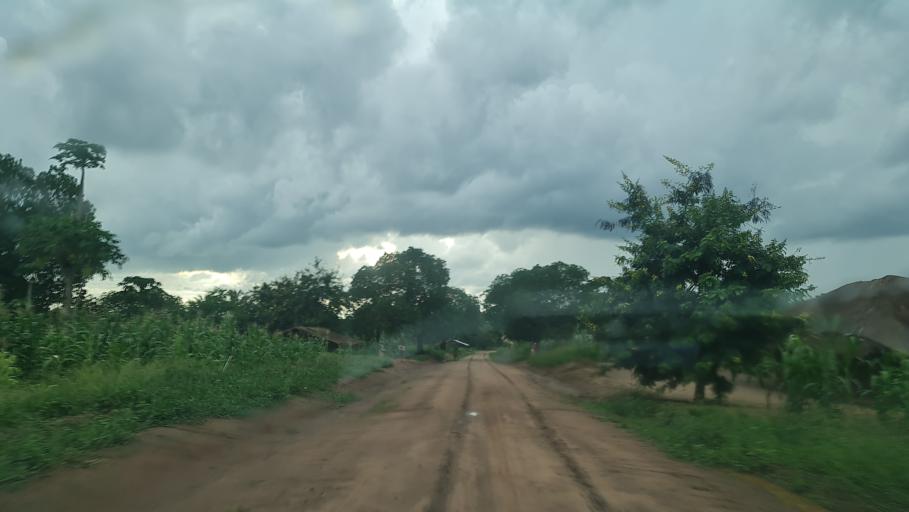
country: MZ
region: Nampula
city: Nacala
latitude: -13.9847
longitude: 40.4000
